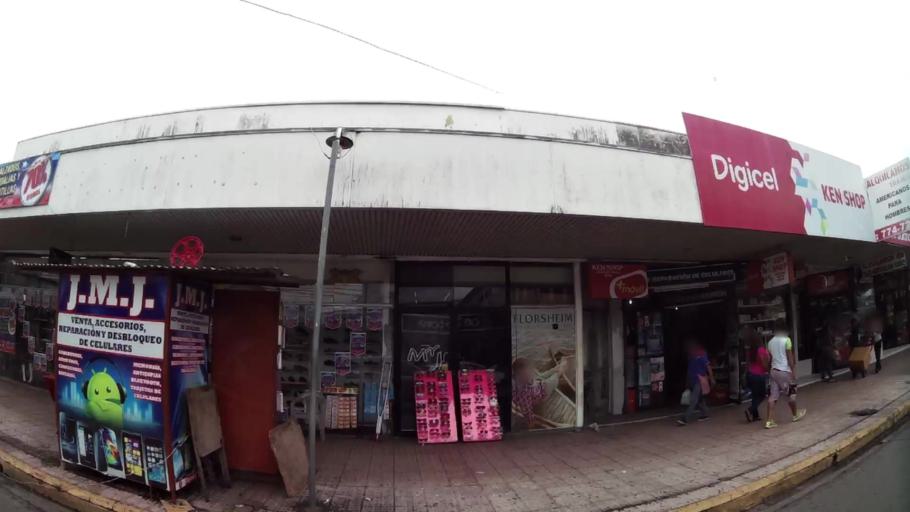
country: PA
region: Chiriqui
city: David
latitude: 8.4292
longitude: -82.4251
